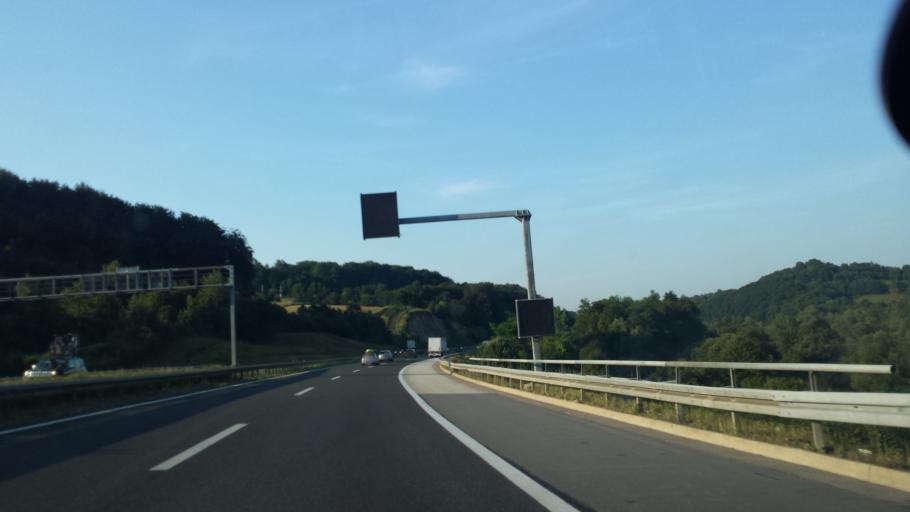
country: HR
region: Karlovacka
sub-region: Grad Karlovac
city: Karlovac
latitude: 45.4961
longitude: 15.4480
